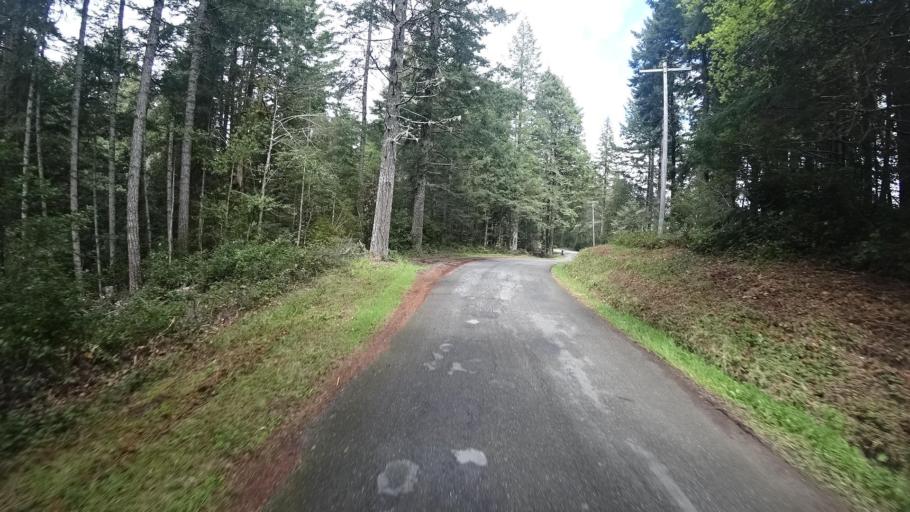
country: US
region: California
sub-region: Humboldt County
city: Blue Lake
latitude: 40.8002
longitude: -123.9840
